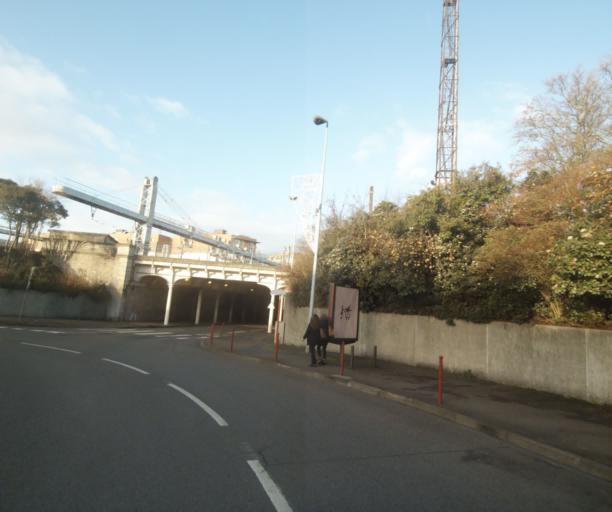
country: FR
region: Pays de la Loire
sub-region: Departement de la Sarthe
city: Le Mans
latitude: 47.9938
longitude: 0.1954
